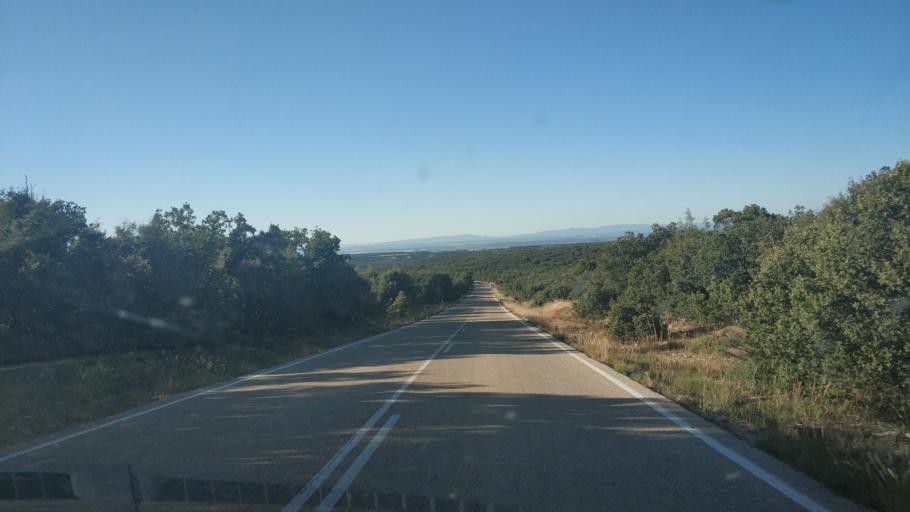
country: ES
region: Castille and Leon
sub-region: Provincia de Soria
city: Montejo de Tiermes
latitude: 41.4070
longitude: -3.2020
